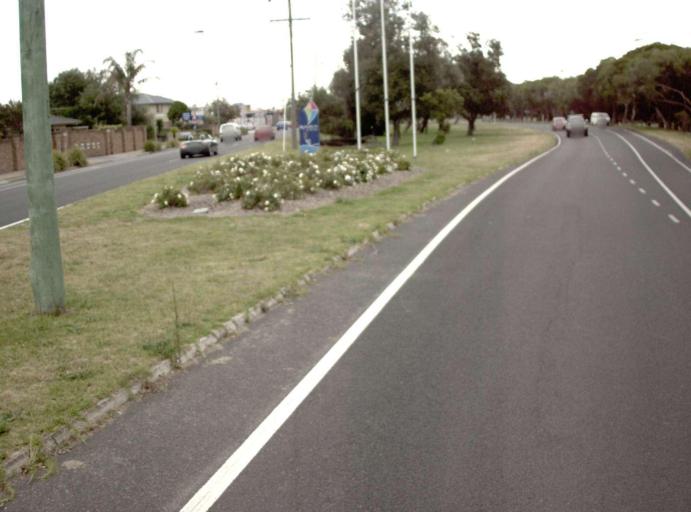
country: AU
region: Victoria
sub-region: Mornington Peninsula
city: Rosebud
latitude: -38.3527
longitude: 144.9158
